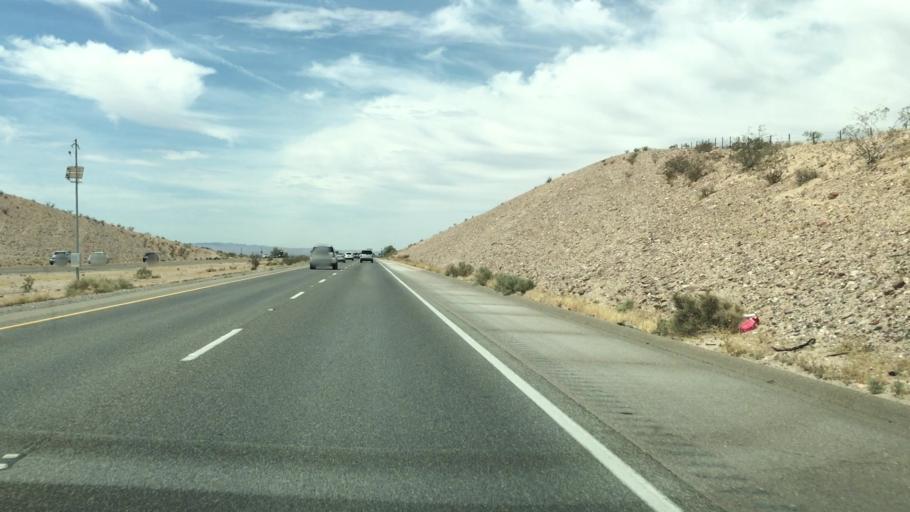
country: US
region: California
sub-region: San Bernardino County
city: Fort Irwin
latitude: 34.9729
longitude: -116.6241
